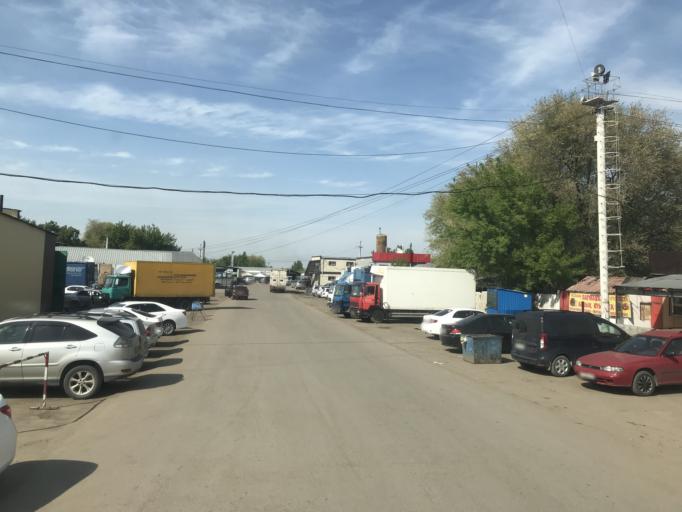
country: KZ
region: Almaty Oblysy
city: Burunday
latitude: 43.2330
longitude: 76.7699
